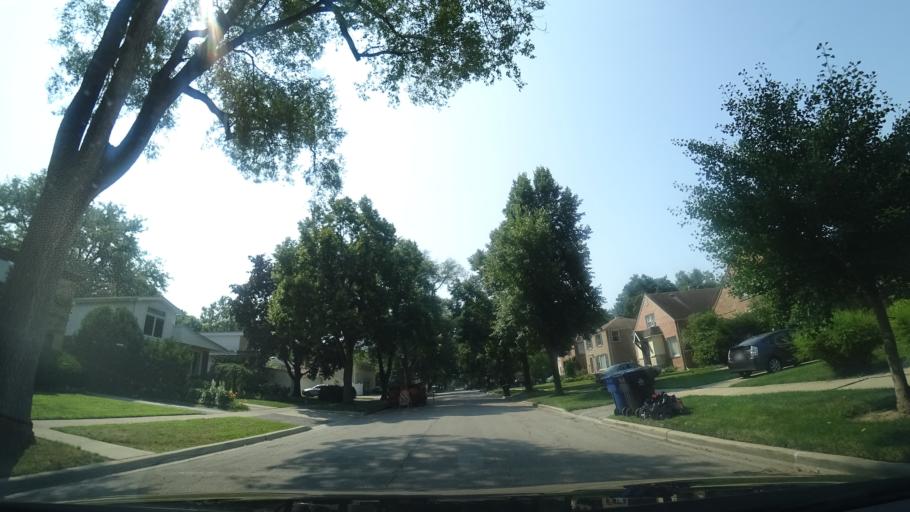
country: US
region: Illinois
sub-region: Cook County
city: Evanston
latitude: 42.0258
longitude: -87.6964
